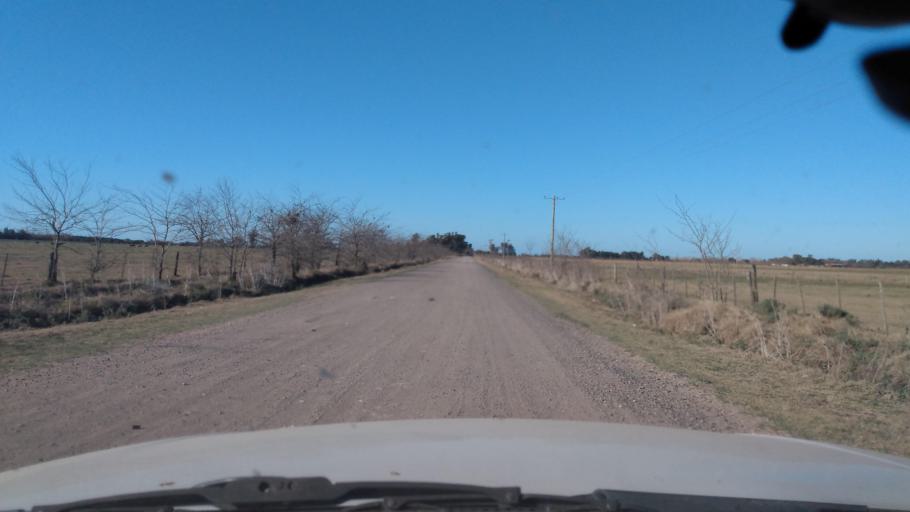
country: AR
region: Buenos Aires
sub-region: Partido de Mercedes
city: Mercedes
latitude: -34.6119
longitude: -59.3192
